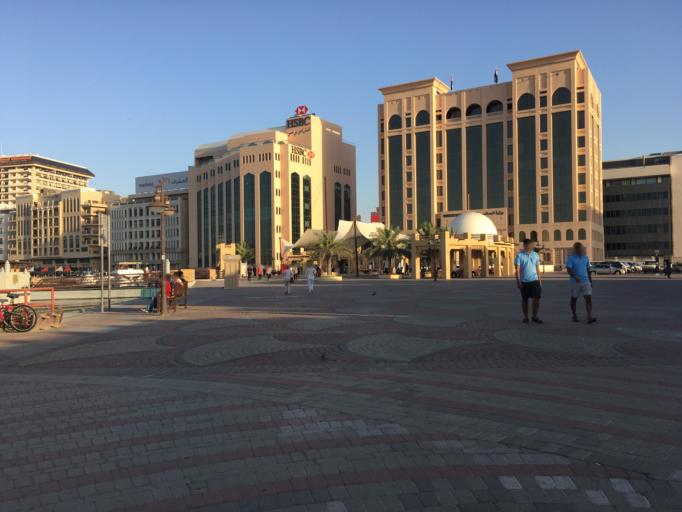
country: AE
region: Ash Shariqah
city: Sharjah
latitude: 25.2658
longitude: 55.2904
